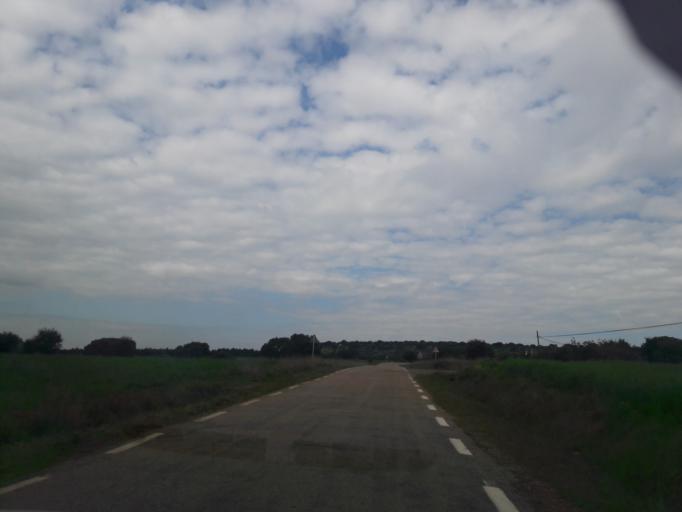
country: ES
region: Castille and Leon
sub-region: Provincia de Salamanca
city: Serradilla del Arroyo
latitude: 40.5222
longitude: -6.3768
